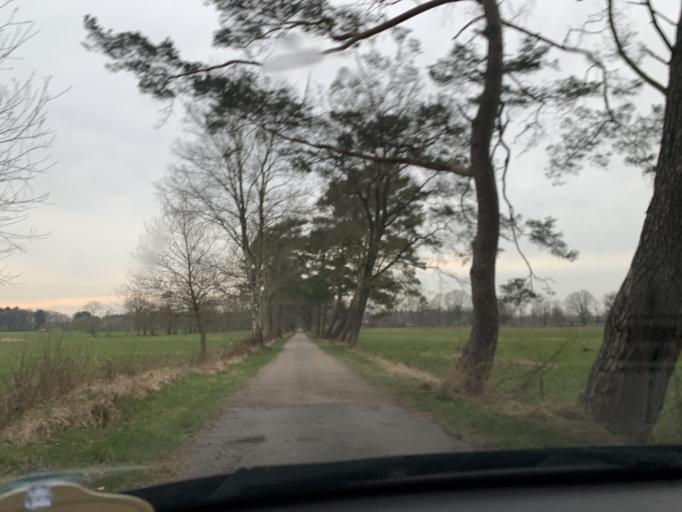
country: DE
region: Lower Saxony
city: Bad Zwischenahn
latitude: 53.2176
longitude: 7.9819
